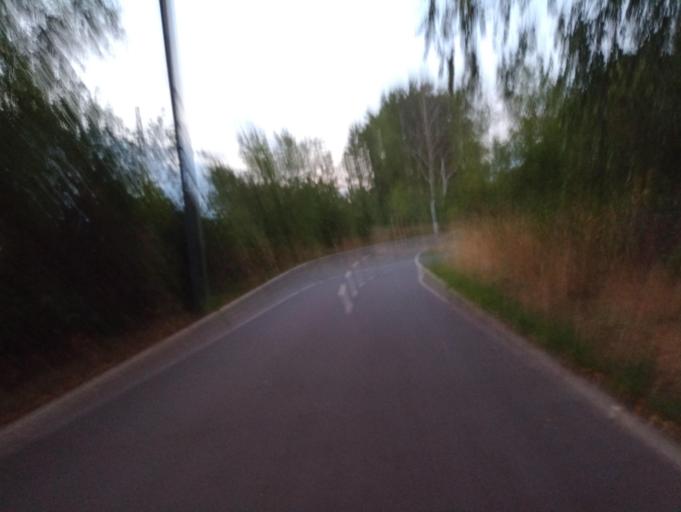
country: DE
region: Hesse
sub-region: Regierungsbezirk Darmstadt
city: Egelsbach
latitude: 49.9761
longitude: 8.6547
